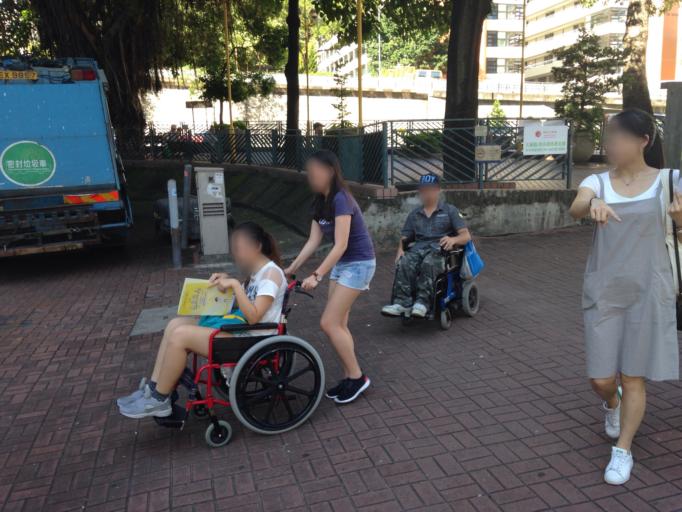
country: HK
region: Sham Shui Po
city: Sham Shui Po
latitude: 22.3336
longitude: 114.1629
